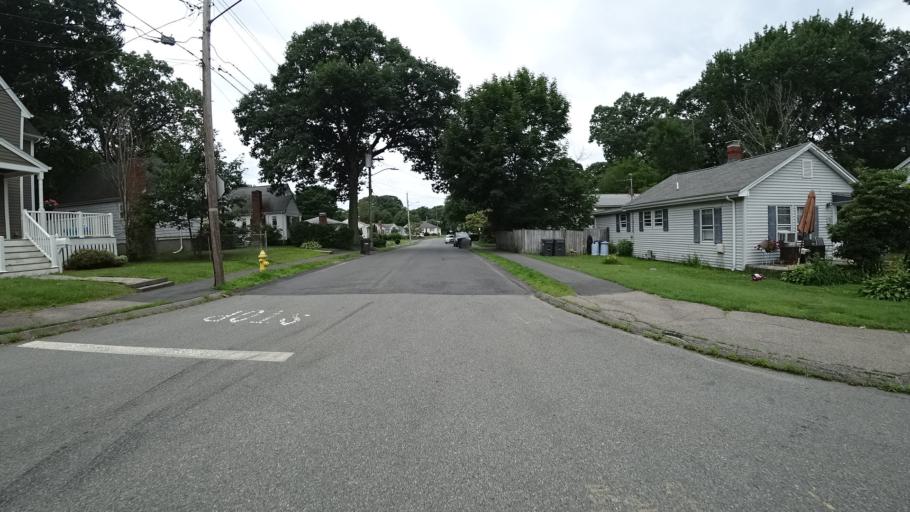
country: US
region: Massachusetts
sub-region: Norfolk County
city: Dedham
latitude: 42.2322
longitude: -71.1510
